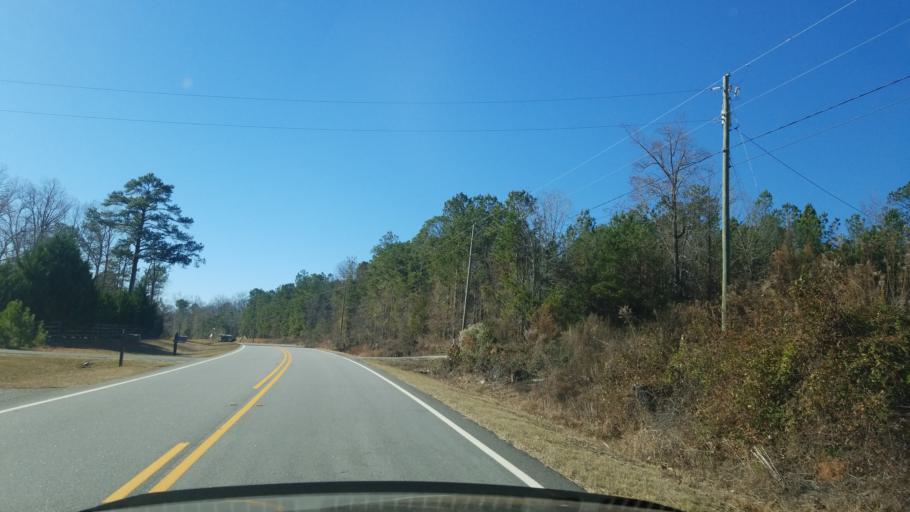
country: US
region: Georgia
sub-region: Harris County
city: Hamilton
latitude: 32.6317
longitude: -84.7627
